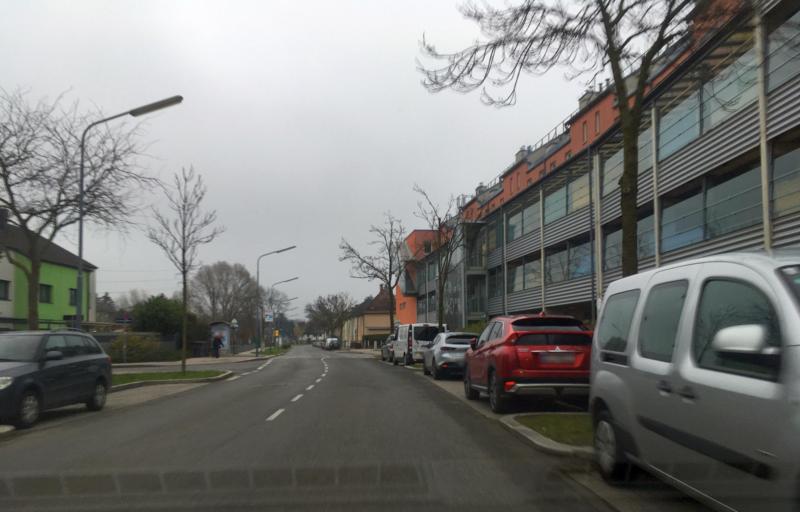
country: AT
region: Lower Austria
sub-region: Politischer Bezirk Ganserndorf
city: Gross-Enzersdorf
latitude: 48.2132
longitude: 16.4753
